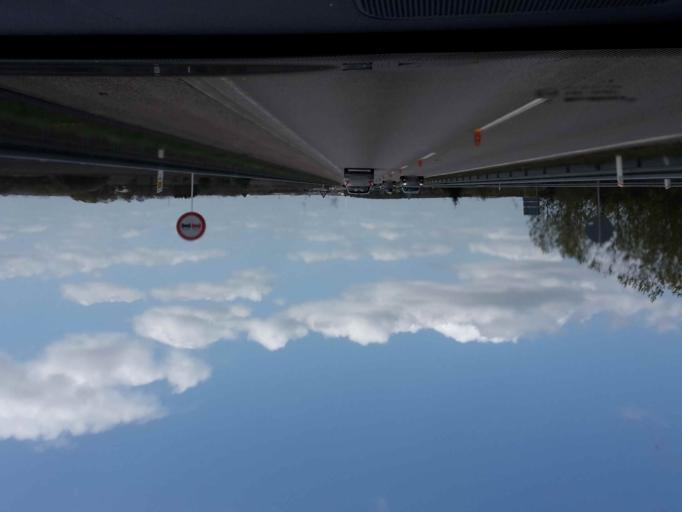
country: DK
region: South Denmark
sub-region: Vejen Kommune
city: Holsted
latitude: 55.5201
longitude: 8.8661
